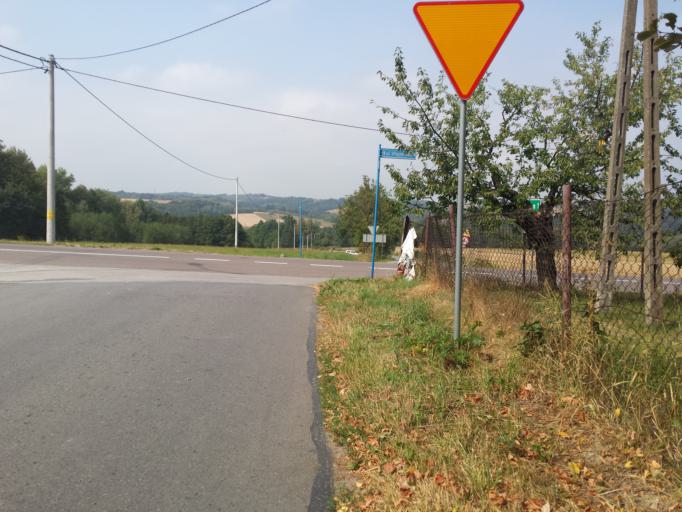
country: PL
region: Subcarpathian Voivodeship
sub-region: Powiat rzeszowski
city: Dynow
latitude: 49.8278
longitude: 22.2041
